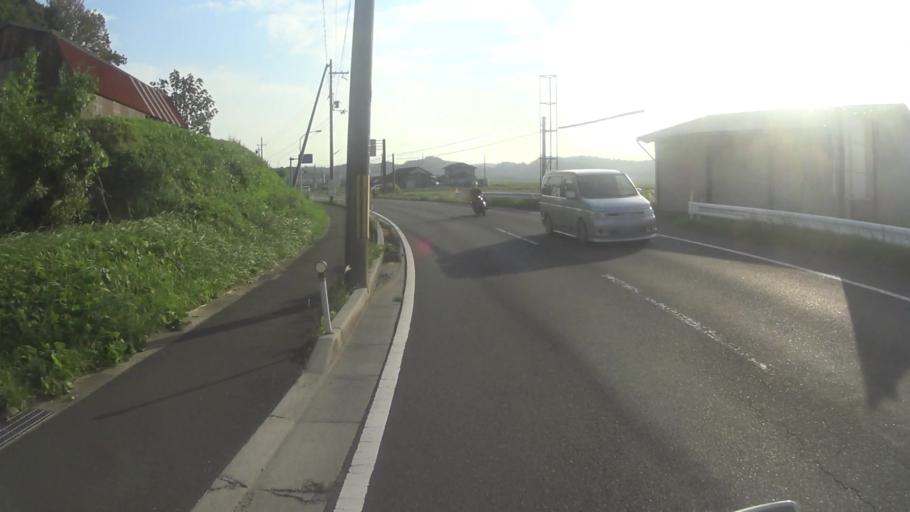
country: JP
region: Kyoto
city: Miyazu
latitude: 35.6709
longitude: 135.0922
